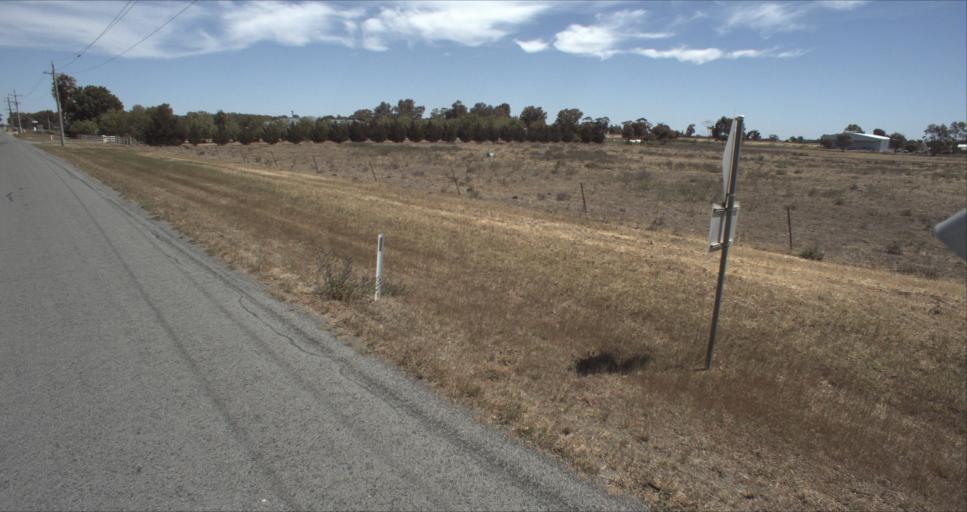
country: AU
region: New South Wales
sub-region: Leeton
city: Leeton
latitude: -34.5737
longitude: 146.4218
